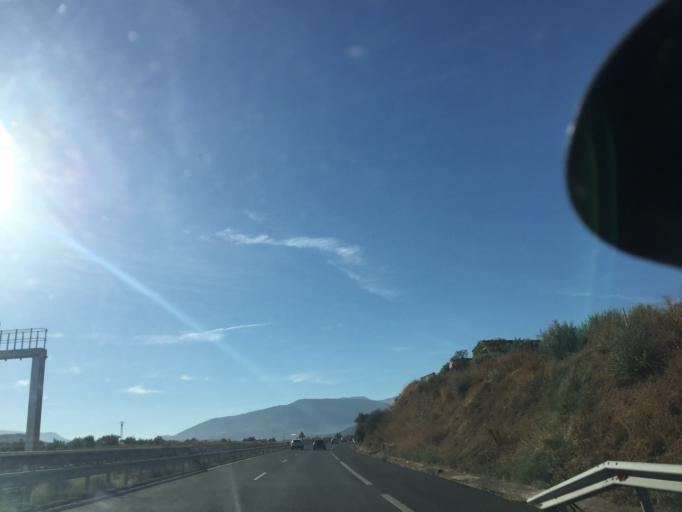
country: ES
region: Andalusia
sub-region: Provincia de Jaen
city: Jaen
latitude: 37.8046
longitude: -3.7602
